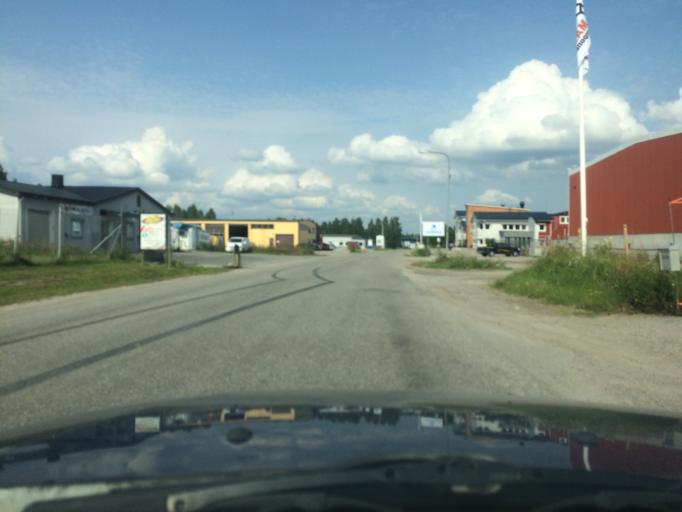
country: SE
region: Norrbotten
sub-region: Pitea Kommun
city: Bergsviken
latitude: 65.3364
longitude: 21.4157
